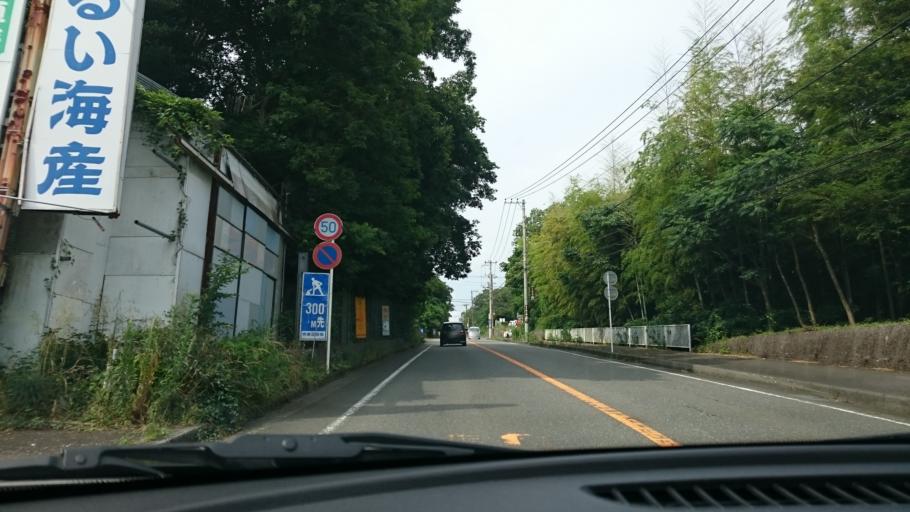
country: JP
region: Shizuoka
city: Ito
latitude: 34.8931
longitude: 139.1179
